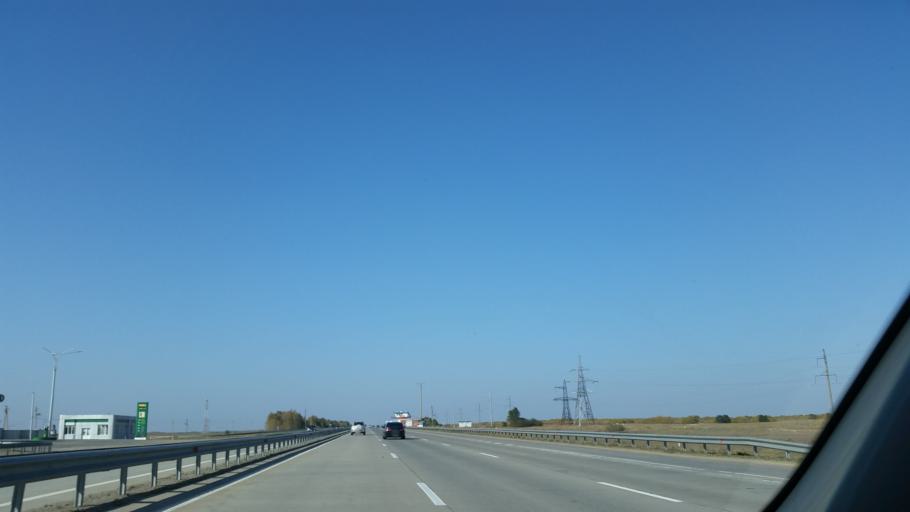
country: KZ
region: Astana Qalasy
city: Astana
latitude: 51.3009
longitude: 71.3556
